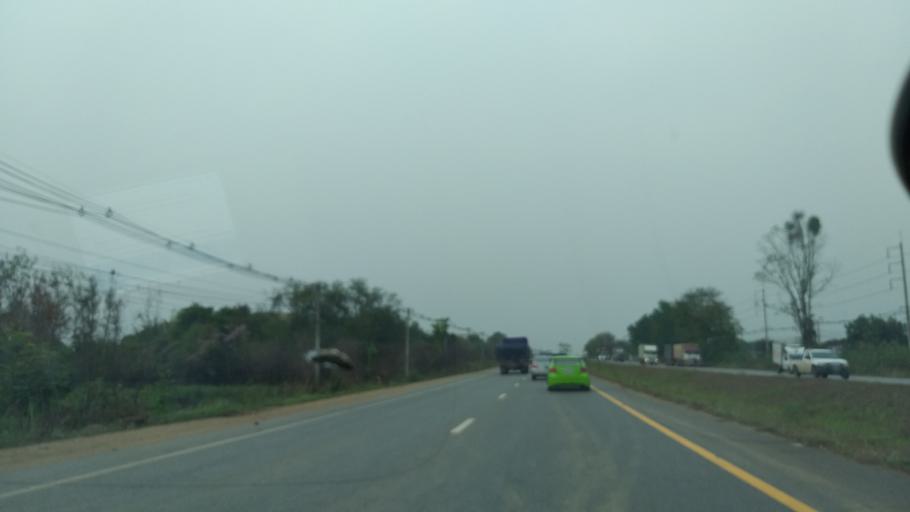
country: TH
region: Chon Buri
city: Ko Chan
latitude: 13.3444
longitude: 101.2706
